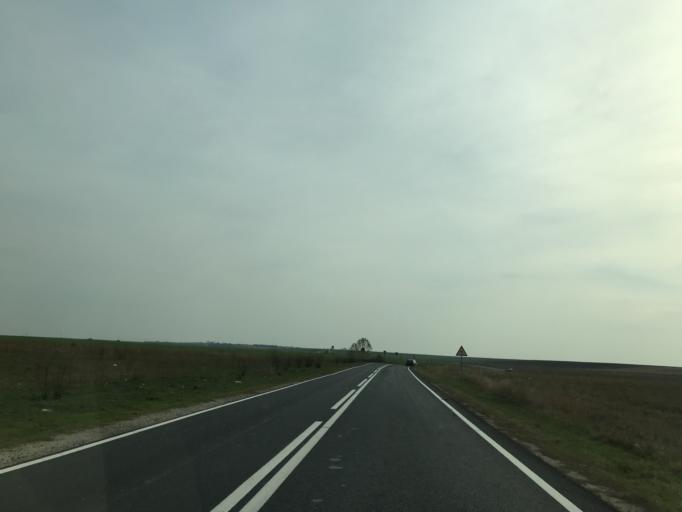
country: RO
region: Olt
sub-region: Comuna Piatra Olt
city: Piatra
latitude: 44.3422
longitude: 24.2955
